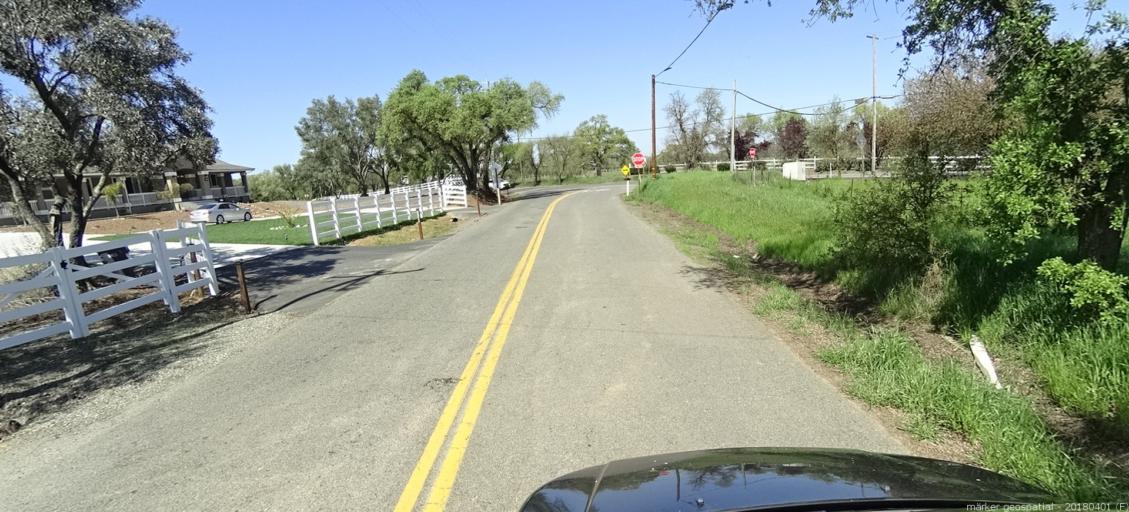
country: US
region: California
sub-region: Sacramento County
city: Wilton
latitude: 38.4115
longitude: -121.2629
